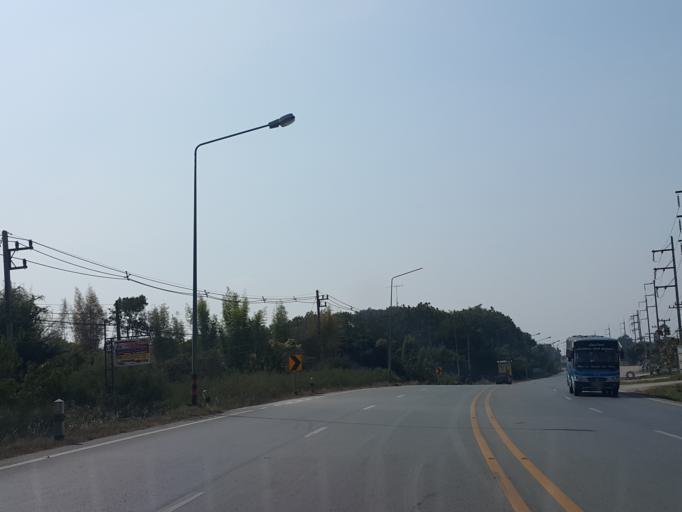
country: TH
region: Chiang Mai
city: Chom Thong
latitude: 18.3444
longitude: 98.6800
